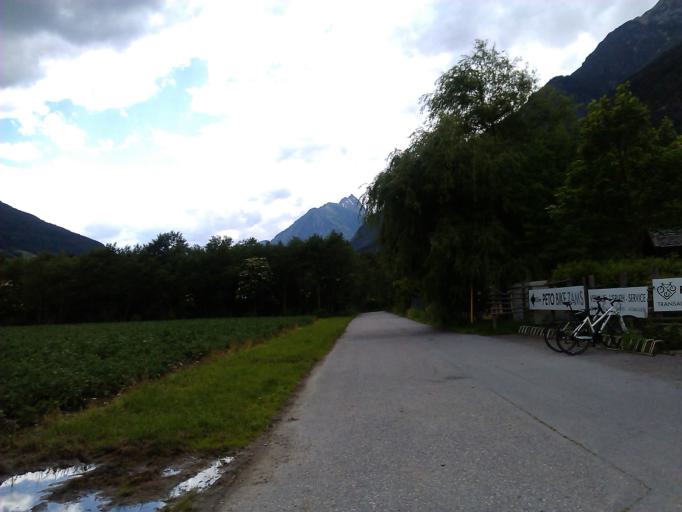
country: AT
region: Tyrol
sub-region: Politischer Bezirk Imst
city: Imsterberg
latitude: 47.2127
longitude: 10.6967
